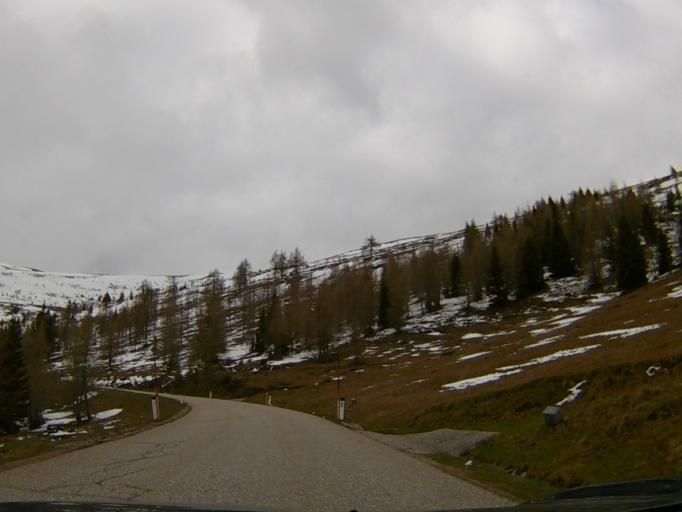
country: AT
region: Carinthia
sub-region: Politischer Bezirk Spittal an der Drau
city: Spittal an der Drau
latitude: 46.7521
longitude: 13.4763
